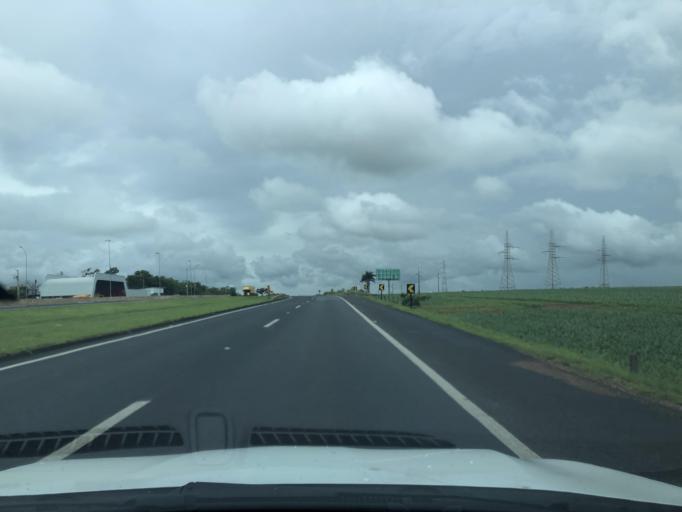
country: BR
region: Minas Gerais
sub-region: Uberlandia
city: Uberlandia
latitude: -19.0207
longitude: -48.2054
